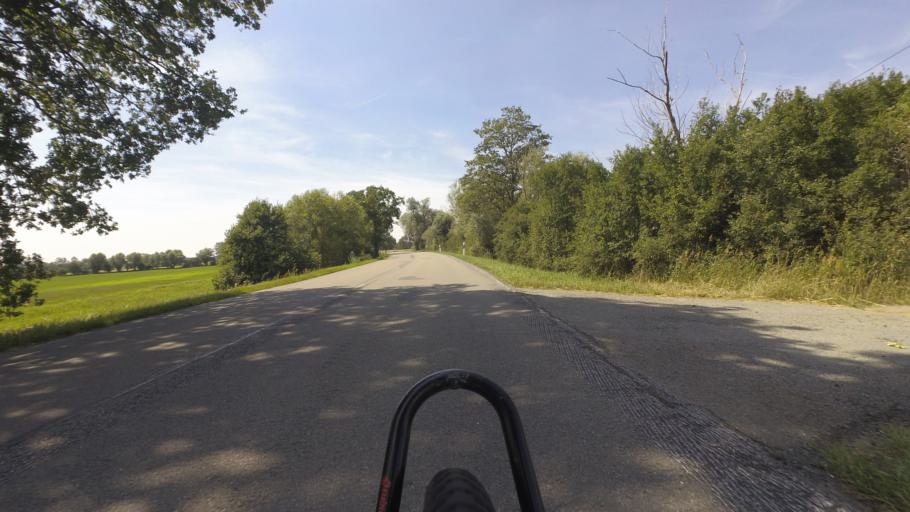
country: DE
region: Saxony-Anhalt
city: Kamern
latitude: 52.7655
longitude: 12.1965
